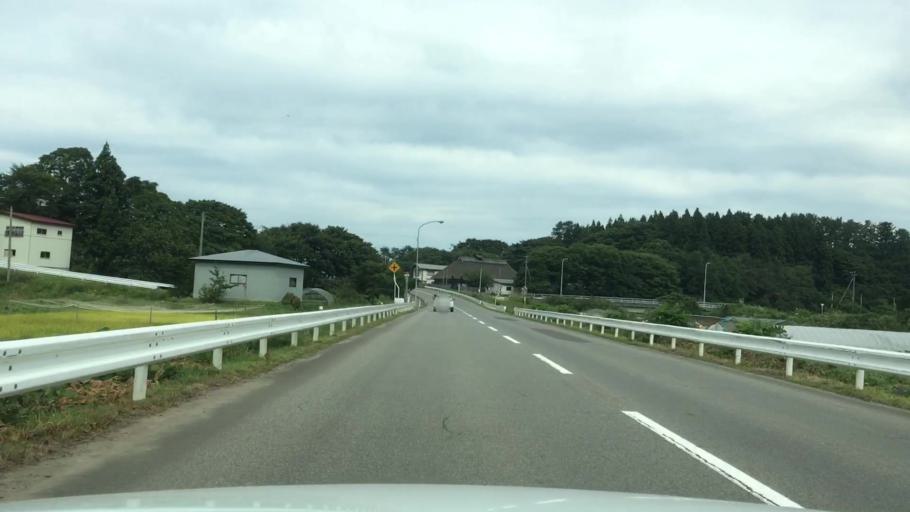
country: JP
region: Aomori
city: Shimokizukuri
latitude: 40.7557
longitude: 140.2307
